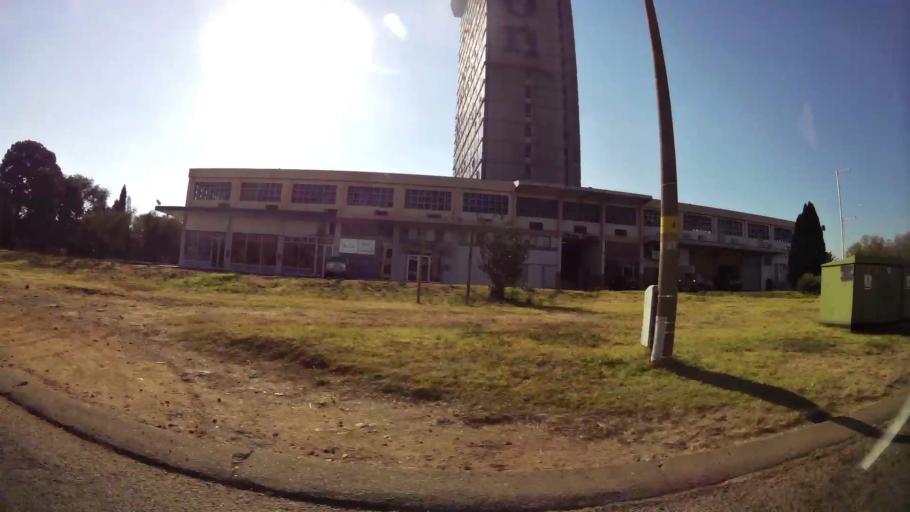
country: ZA
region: Gauteng
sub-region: City of Johannesburg Metropolitan Municipality
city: Modderfontein
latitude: -26.1599
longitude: 28.1562
